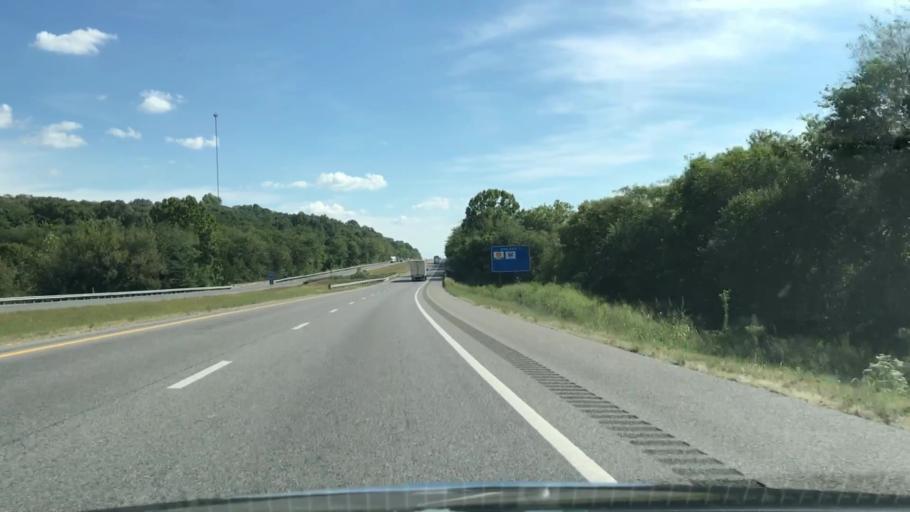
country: US
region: Alabama
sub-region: Limestone County
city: Ardmore
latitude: 35.0338
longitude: -86.8790
